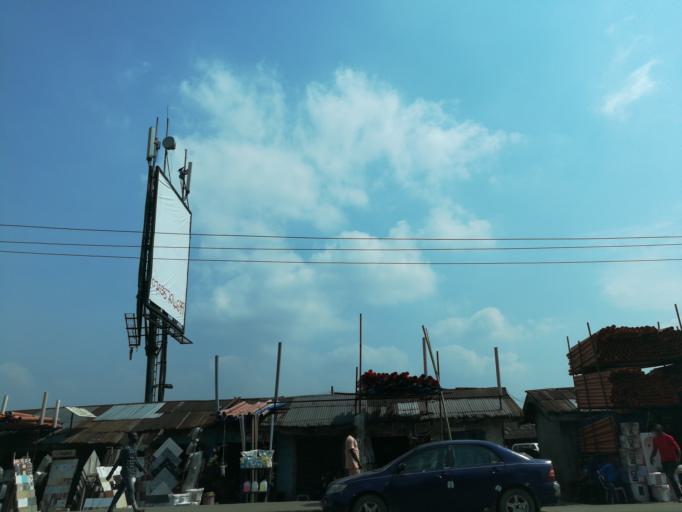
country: NG
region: Rivers
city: Port Harcourt
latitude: 4.8085
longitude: 6.9857
